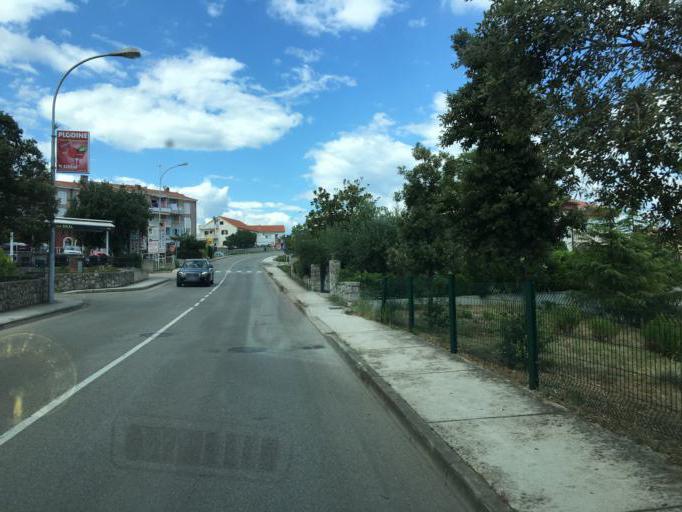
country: HR
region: Primorsko-Goranska
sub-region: Grad Krk
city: Krk
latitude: 45.0304
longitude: 14.5686
